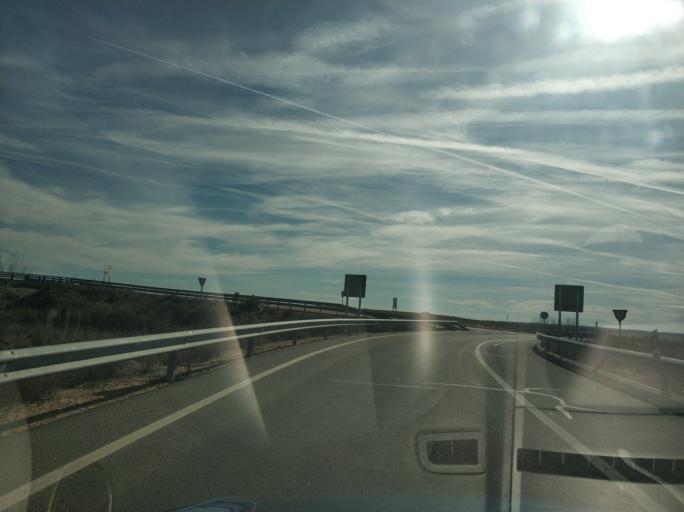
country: ES
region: Castille and Leon
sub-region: Provincia de Zamora
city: Cuelgamures
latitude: 41.2640
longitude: -5.7050
